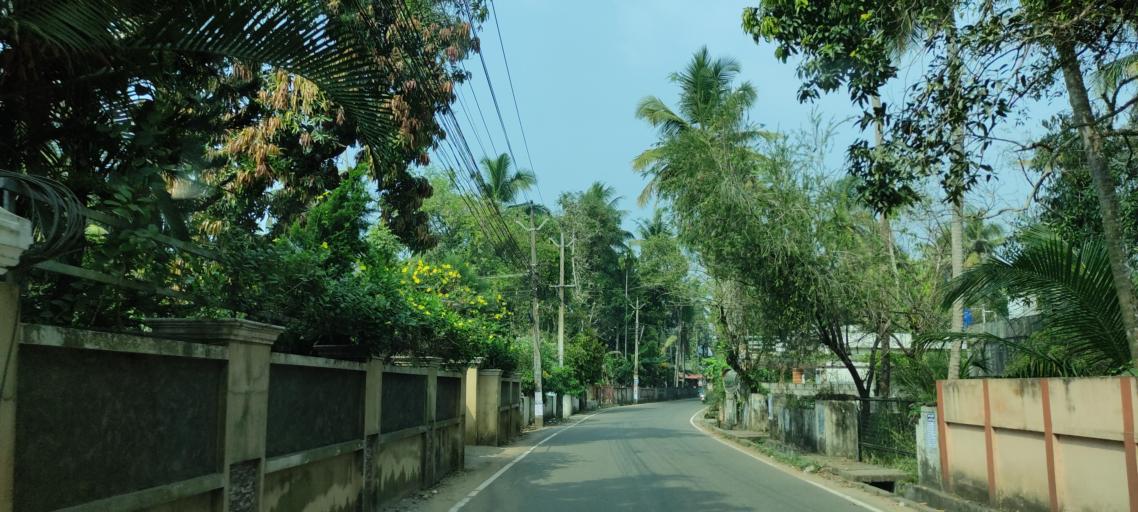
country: IN
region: Kerala
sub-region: Kottayam
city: Vaikam
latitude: 9.7574
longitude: 76.4019
